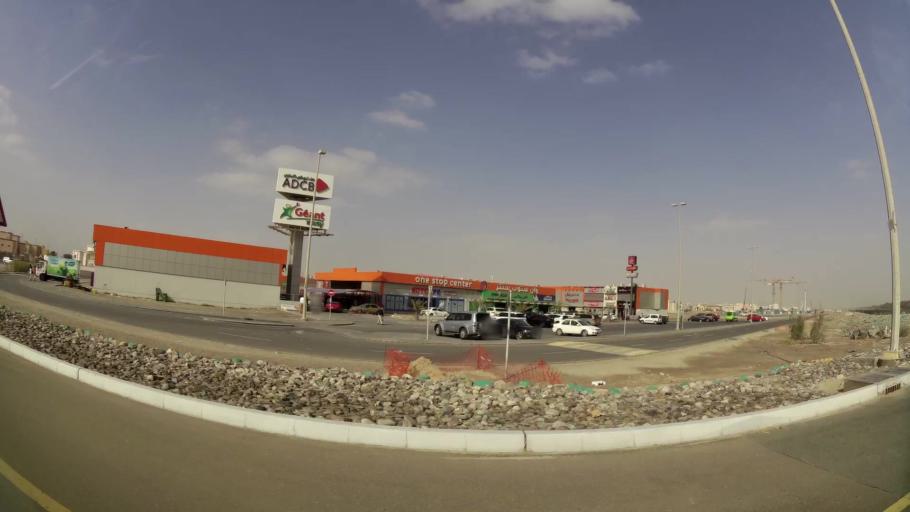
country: AE
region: Abu Dhabi
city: Abu Dhabi
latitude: 24.3997
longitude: 54.5754
